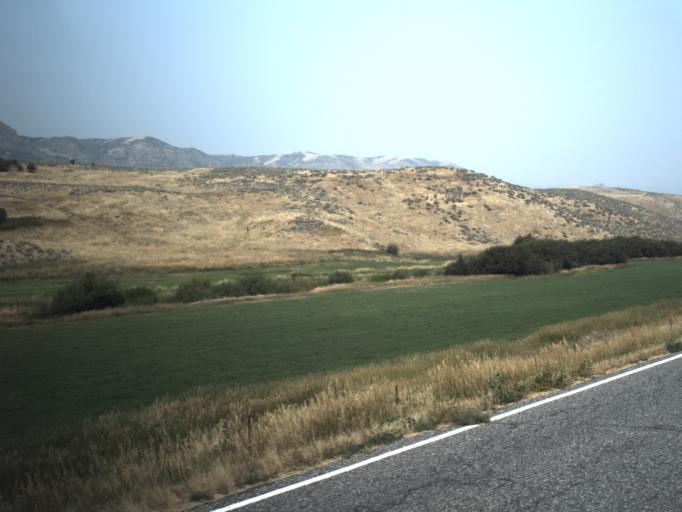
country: US
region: Utah
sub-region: Summit County
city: Coalville
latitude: 40.9967
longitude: -111.5237
